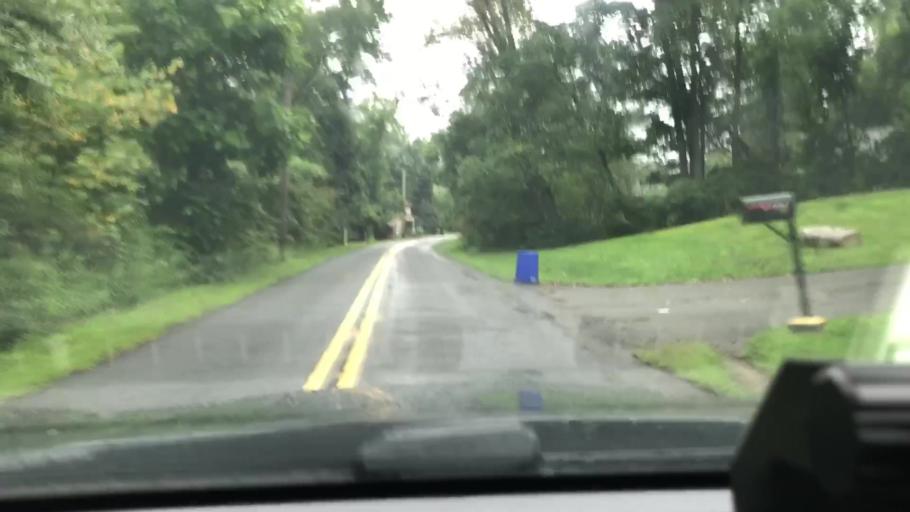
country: US
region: Pennsylvania
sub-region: Lehigh County
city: Macungie
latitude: 40.4679
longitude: -75.5486
